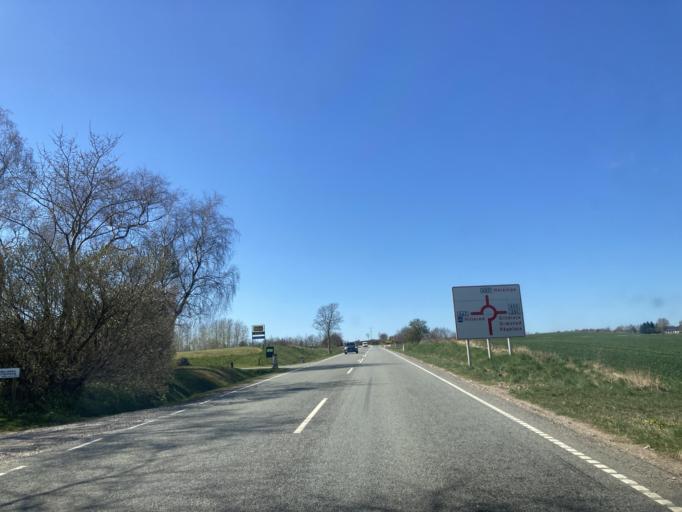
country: DK
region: Capital Region
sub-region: Gribskov Kommune
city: Helsinge
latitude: 56.0055
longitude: 12.2442
